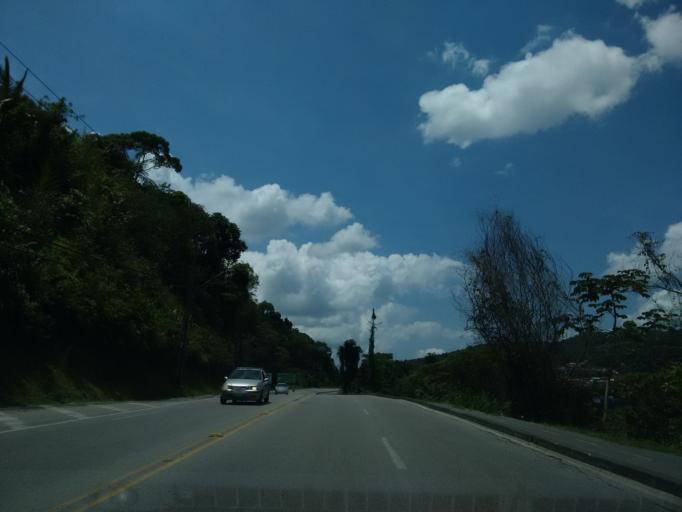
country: BR
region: Santa Catarina
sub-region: Blumenau
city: Blumenau
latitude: -26.9116
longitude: -49.0574
